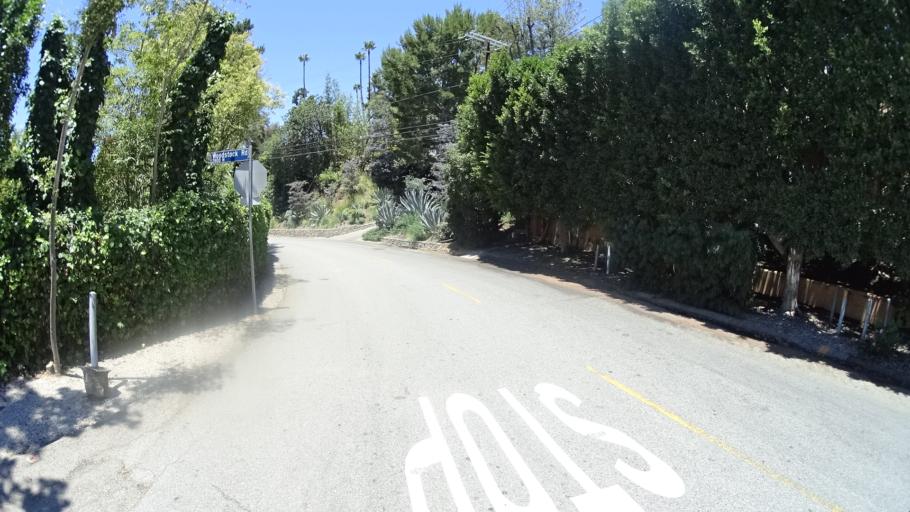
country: US
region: California
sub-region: Los Angeles County
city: Universal City
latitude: 34.1230
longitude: -118.3716
